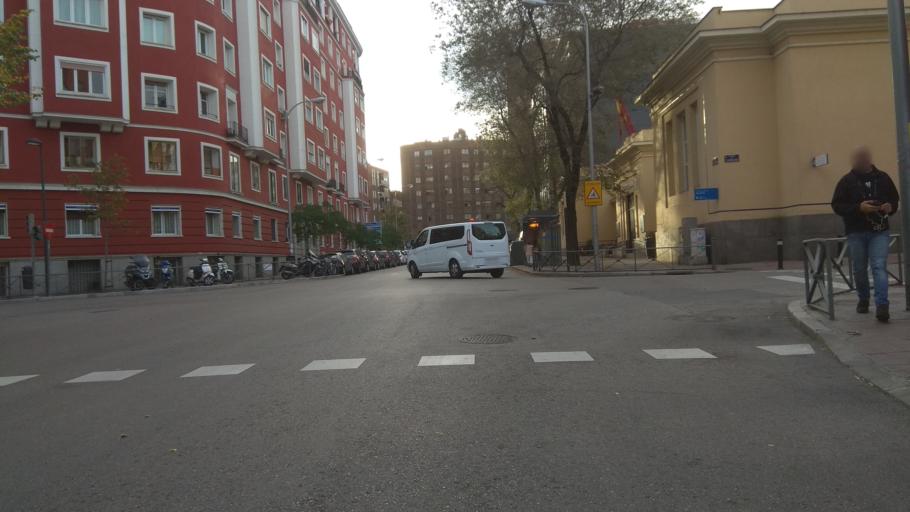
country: ES
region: Madrid
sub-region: Provincia de Madrid
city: Salamanca
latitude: 40.4320
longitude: -3.6698
